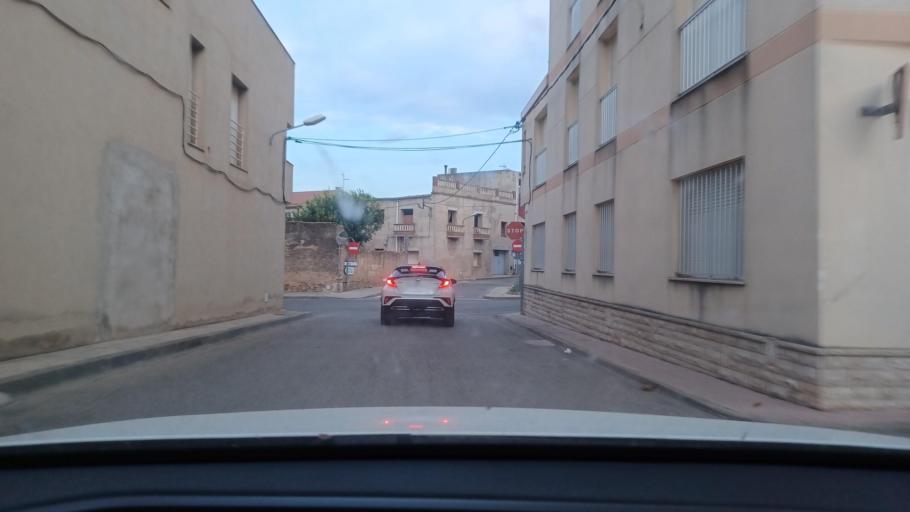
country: ES
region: Catalonia
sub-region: Provincia de Tarragona
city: Santa Barbara
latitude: 40.7140
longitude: 0.4897
